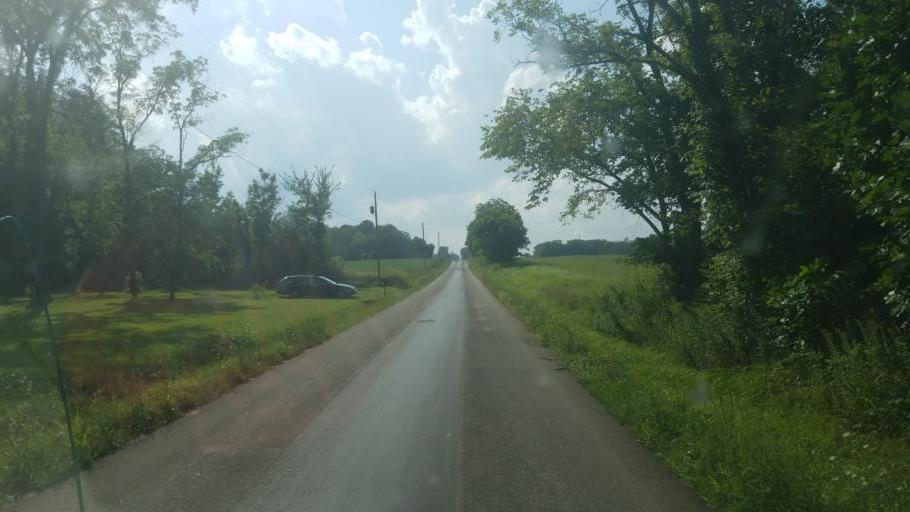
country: US
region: Ohio
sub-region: Wayne County
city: West Salem
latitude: 40.9524
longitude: -82.0437
